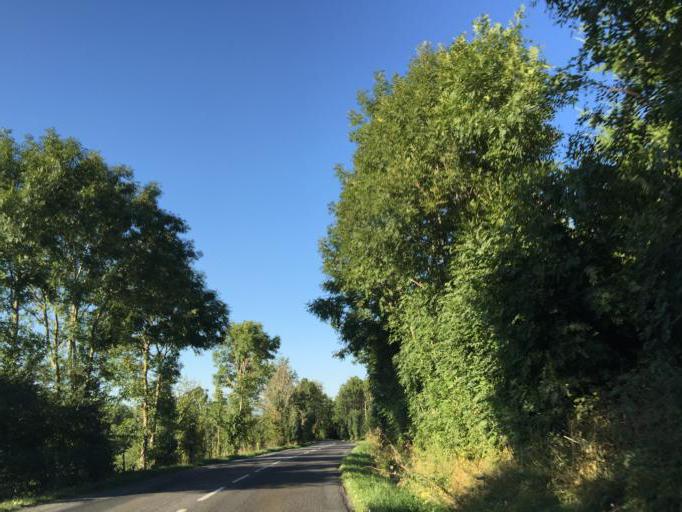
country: FR
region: Midi-Pyrenees
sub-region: Departement de l'Aveyron
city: Salles-Curan
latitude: 44.1458
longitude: 2.8639
